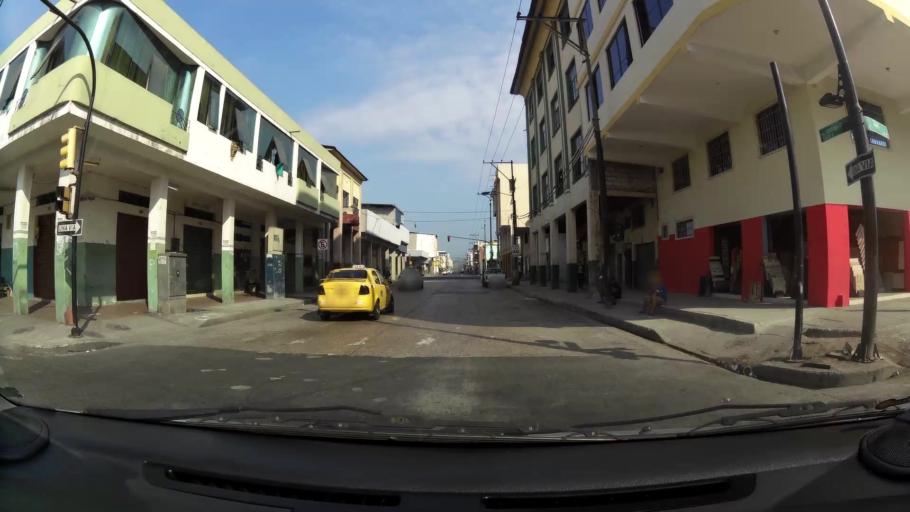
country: EC
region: Guayas
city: Guayaquil
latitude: -2.1950
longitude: -79.8910
